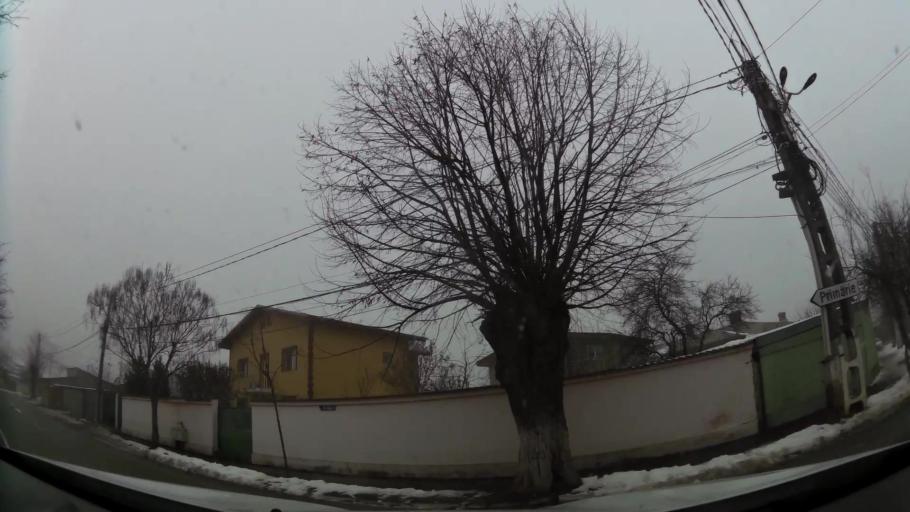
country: RO
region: Ilfov
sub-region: Comuna Chiajna
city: Chiajna
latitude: 44.4587
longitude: 25.9801
